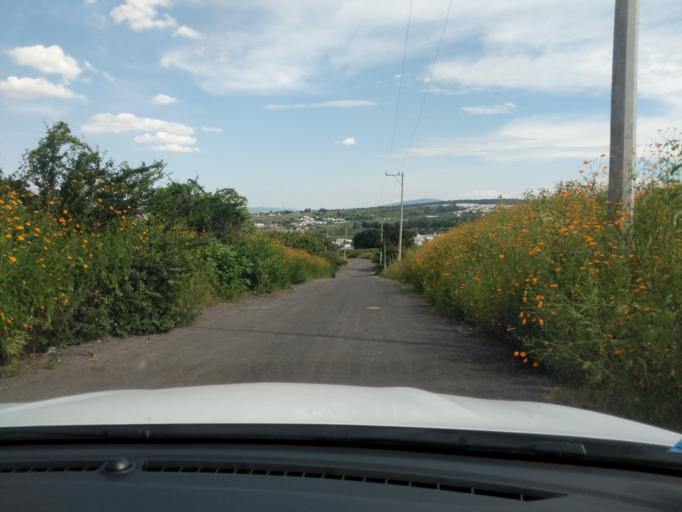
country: MX
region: Jalisco
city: Tonala
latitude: 20.6300
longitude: -103.2191
